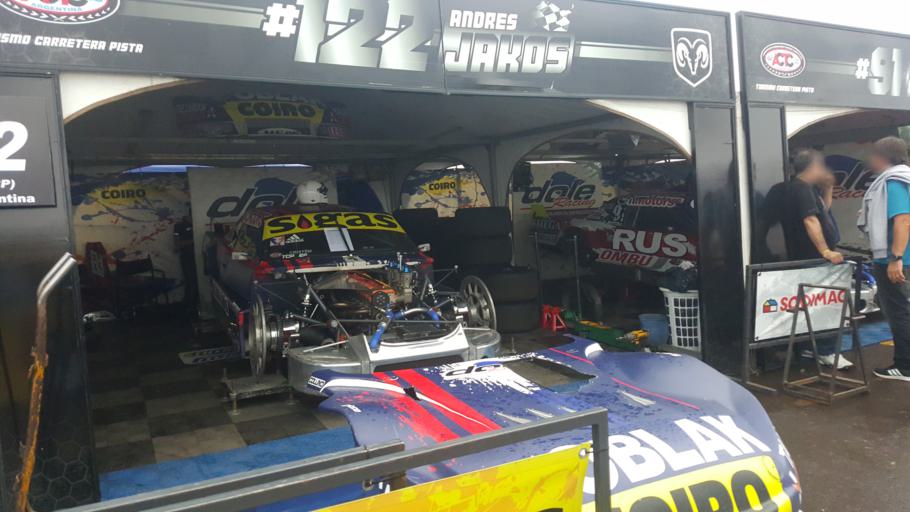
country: AR
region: Misiones
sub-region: Departamento de Capital
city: Posadas
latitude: -27.4391
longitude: -55.9265
